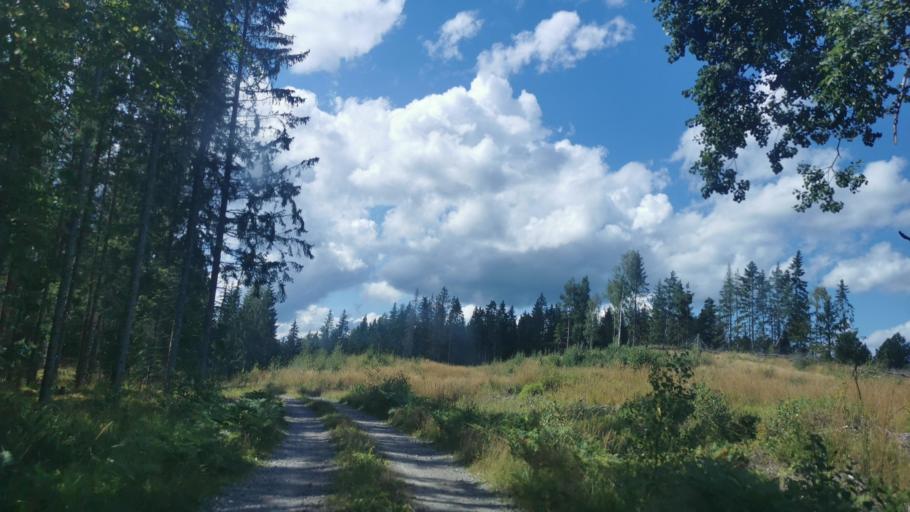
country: SE
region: OEstergoetland
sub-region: Finspangs Kommun
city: Finspang
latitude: 58.8013
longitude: 15.8082
